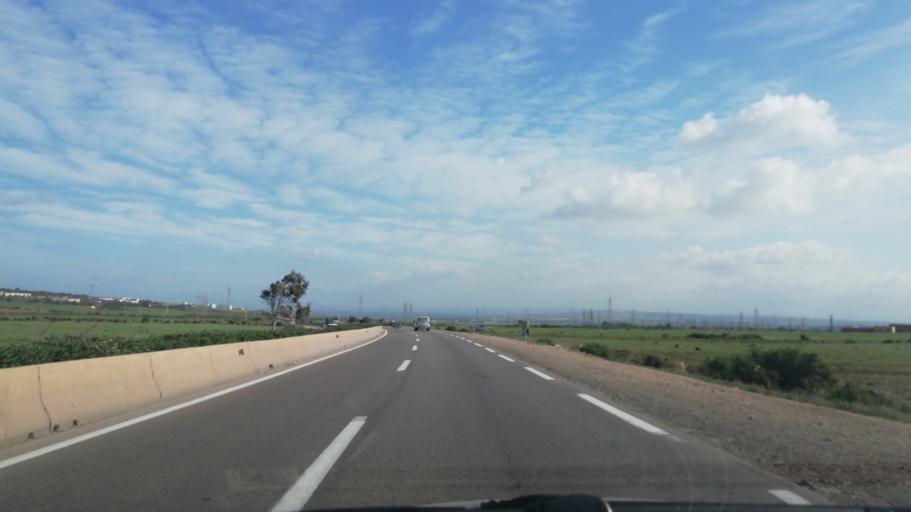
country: DZ
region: Oran
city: Ain el Bya
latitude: 35.7674
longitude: -0.2051
